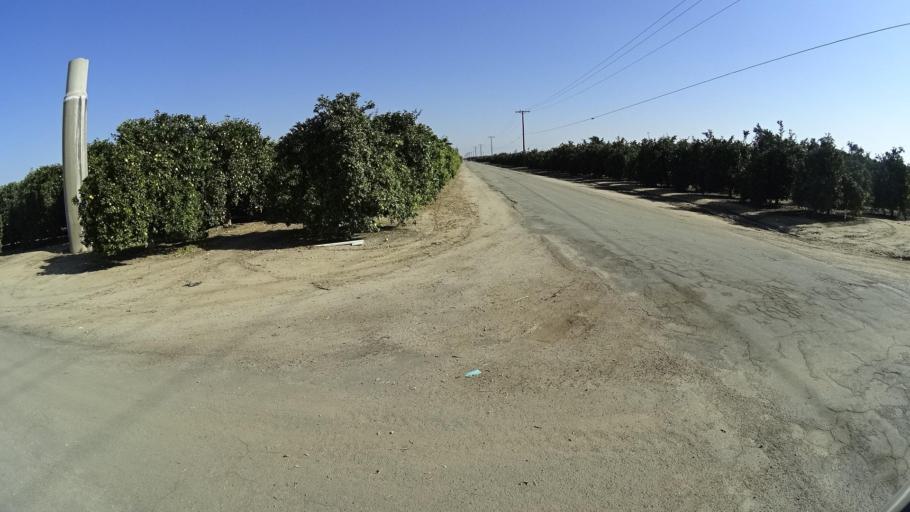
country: US
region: California
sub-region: Tulare County
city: Richgrove
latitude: 35.7326
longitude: -119.1429
